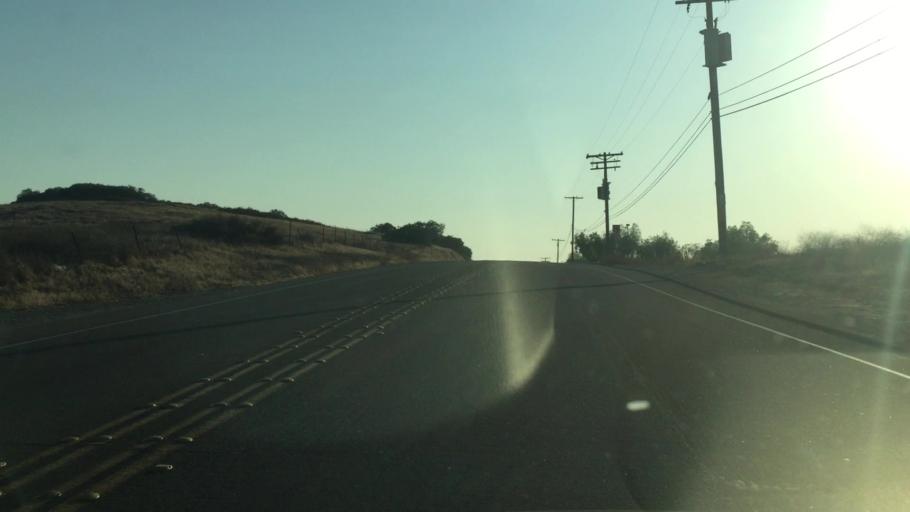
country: US
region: California
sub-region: San Diego County
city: Poway
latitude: 32.9783
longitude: -116.9751
